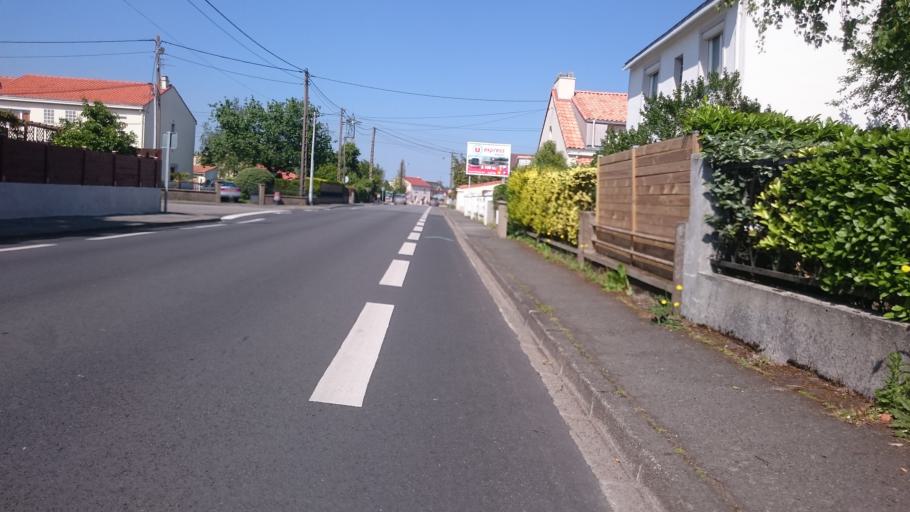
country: FR
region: Pays de la Loire
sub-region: Departement de la Loire-Atlantique
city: Bouguenais
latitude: 47.1814
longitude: -1.5934
